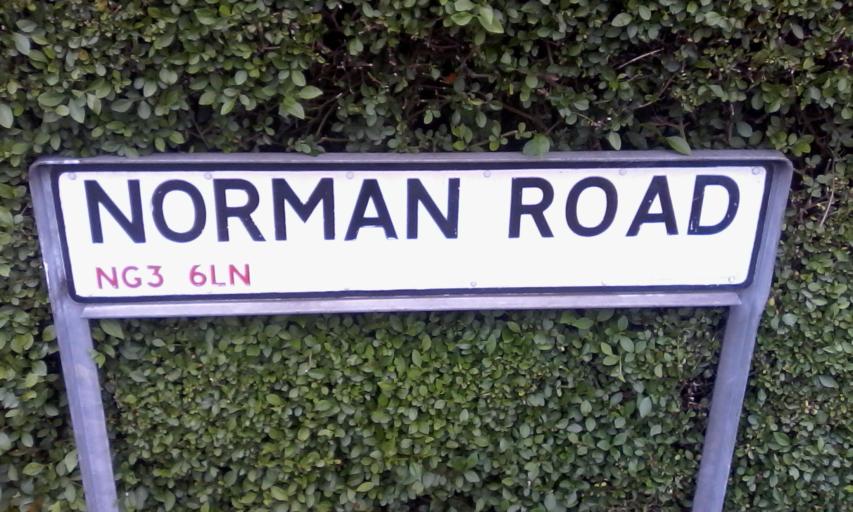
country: GB
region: England
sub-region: Nottinghamshire
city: Arnold
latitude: 52.9719
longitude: -1.1169
